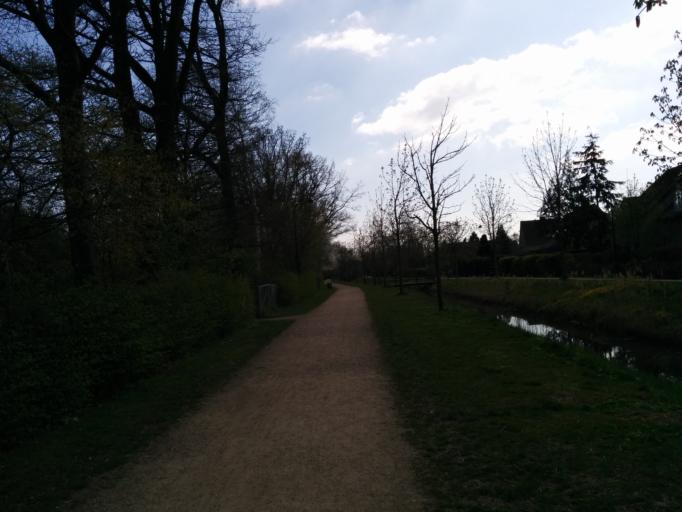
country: DK
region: Capital Region
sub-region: Frederiksberg Kommune
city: Frederiksberg
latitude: 55.7292
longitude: 12.5350
